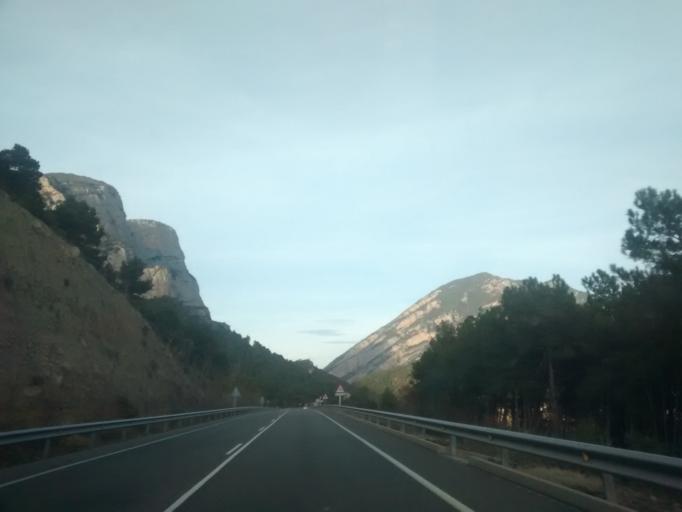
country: ES
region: Catalonia
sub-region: Provincia de Lleida
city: Oliana
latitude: 42.1099
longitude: 1.3003
